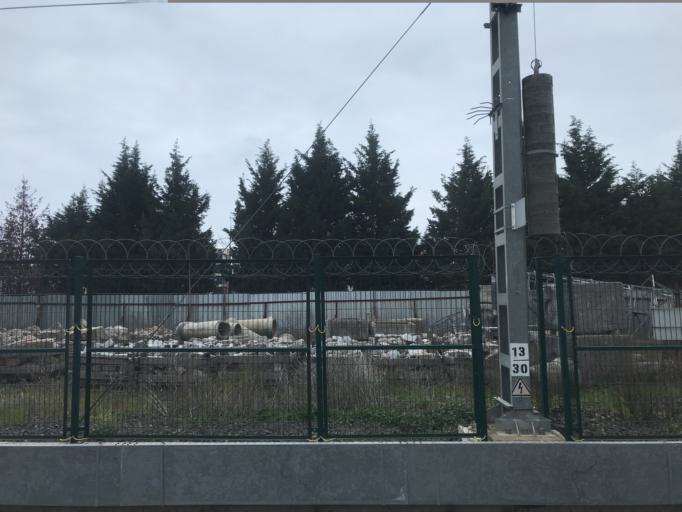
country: TR
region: Istanbul
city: Icmeler
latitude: 40.8451
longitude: 29.3005
